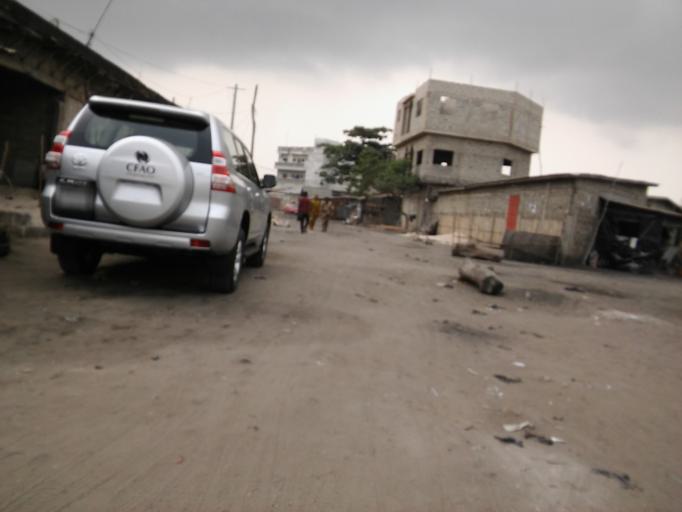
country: BJ
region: Littoral
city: Cotonou
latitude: 6.3835
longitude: 2.4229
